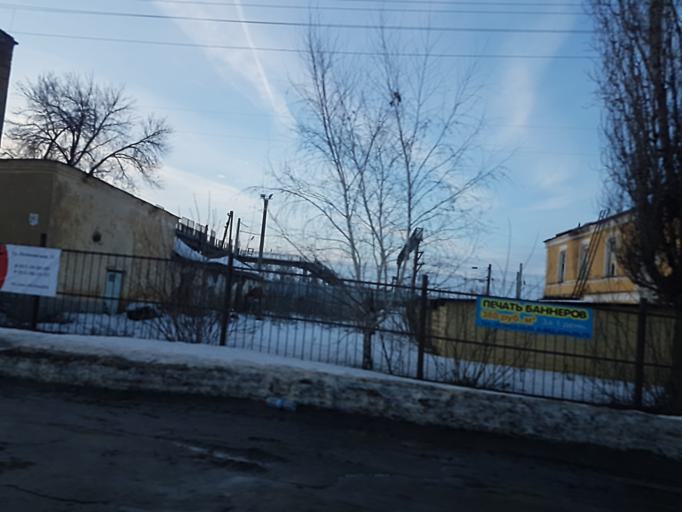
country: RU
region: Tambov
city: Michurinsk
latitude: 52.9019
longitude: 40.4534
